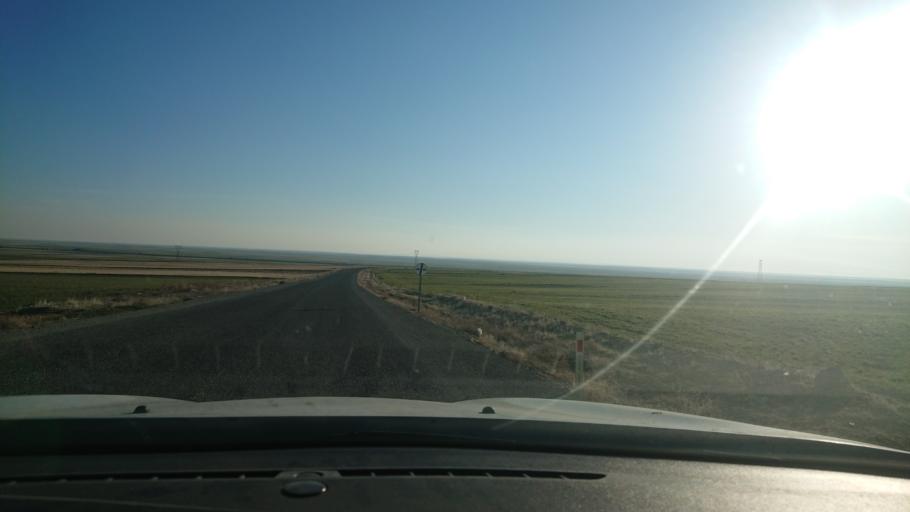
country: TR
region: Aksaray
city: Acipinar
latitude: 38.6775
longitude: 33.7322
